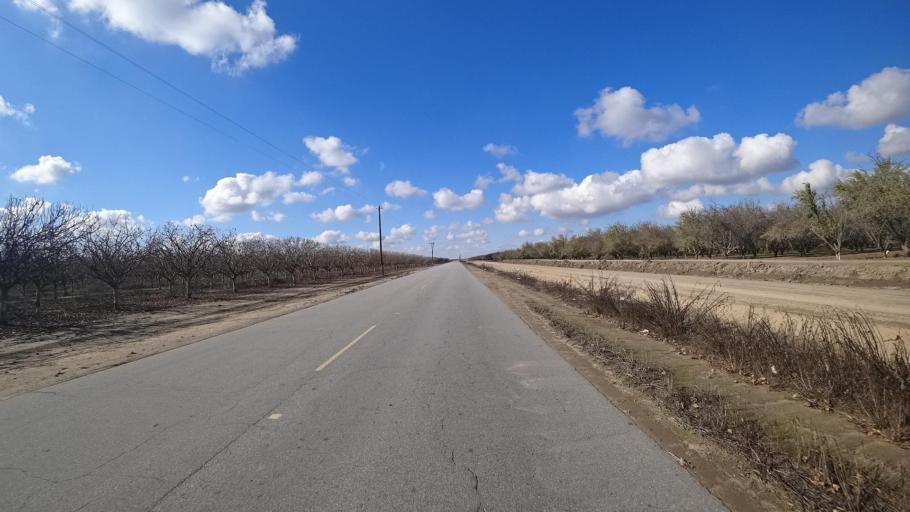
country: US
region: California
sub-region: Kern County
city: Wasco
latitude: 35.6742
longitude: -119.3188
